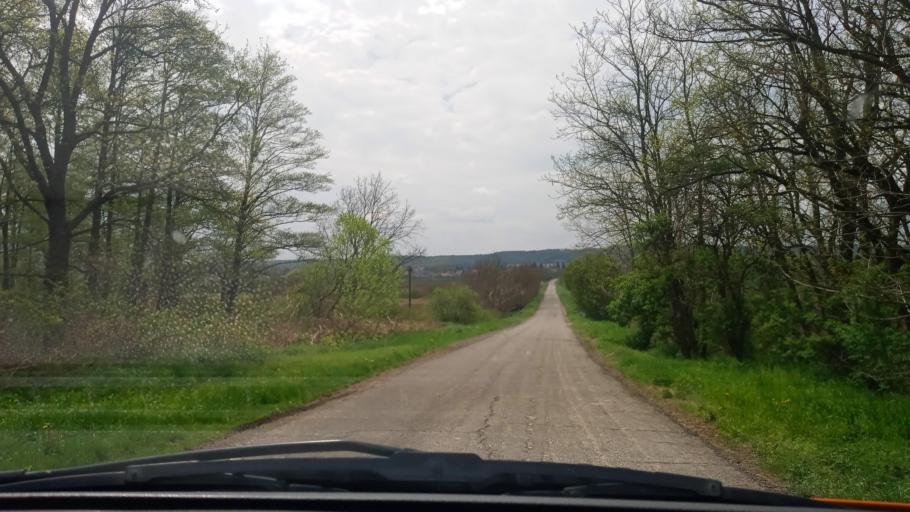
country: HU
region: Baranya
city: Sasd
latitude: 46.2624
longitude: 18.1225
